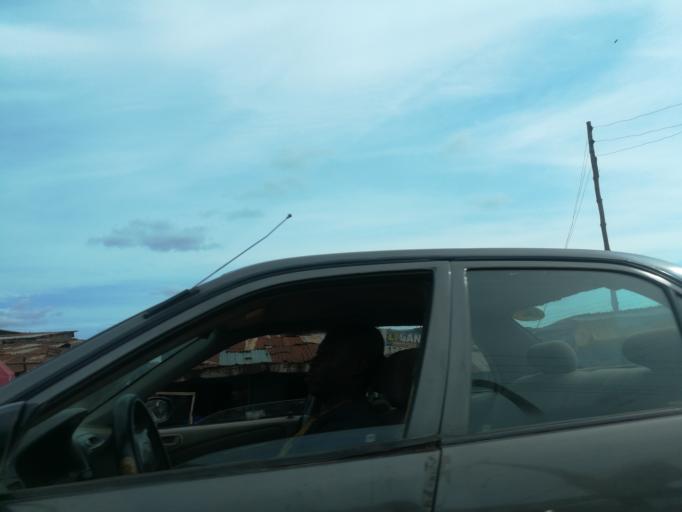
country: NG
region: Oyo
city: Ibadan
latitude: 7.3795
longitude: 3.9463
